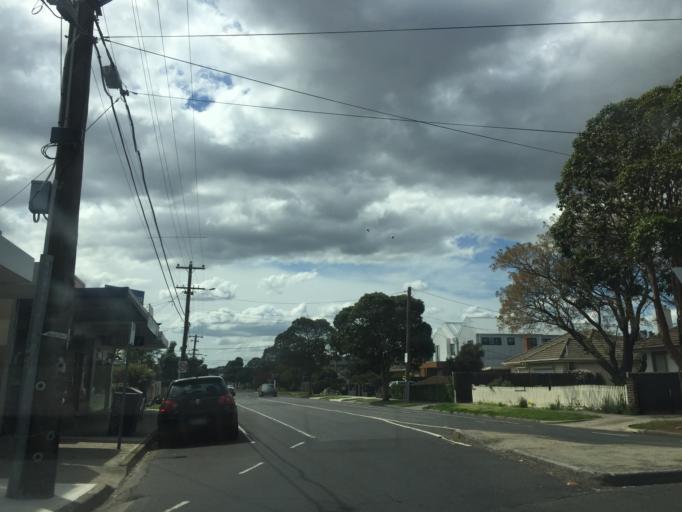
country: AU
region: Victoria
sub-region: Darebin
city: Preston
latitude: -37.7505
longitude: 145.0162
